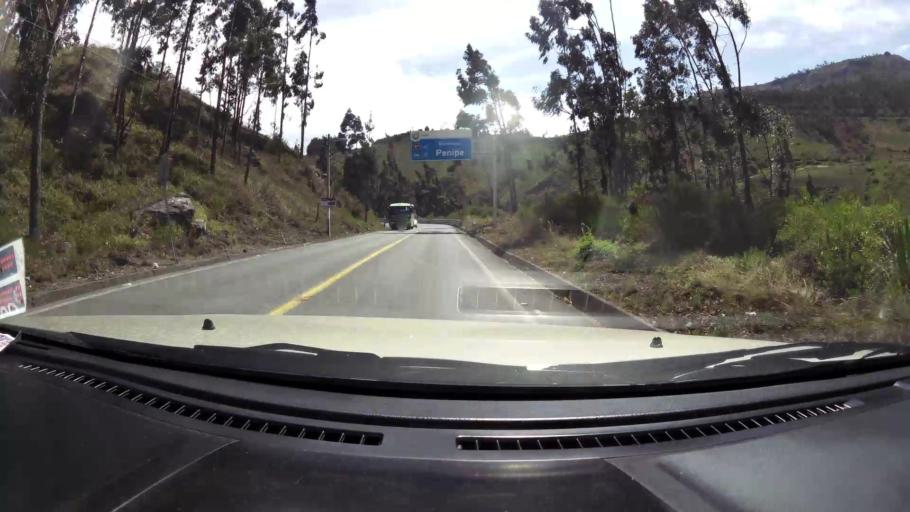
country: EC
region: Chimborazo
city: Guano
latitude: -1.5718
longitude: -78.5353
